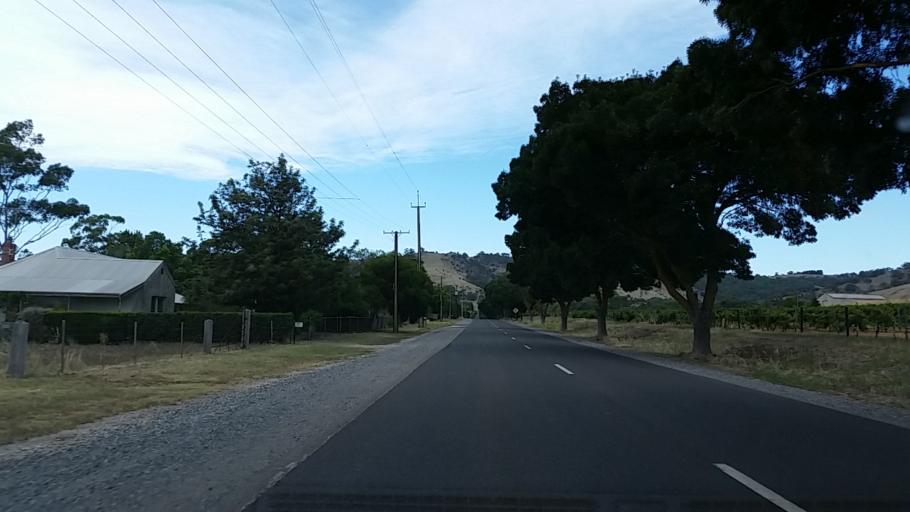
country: AU
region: South Australia
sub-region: Barossa
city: Tanunda
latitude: -34.5398
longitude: 138.9758
